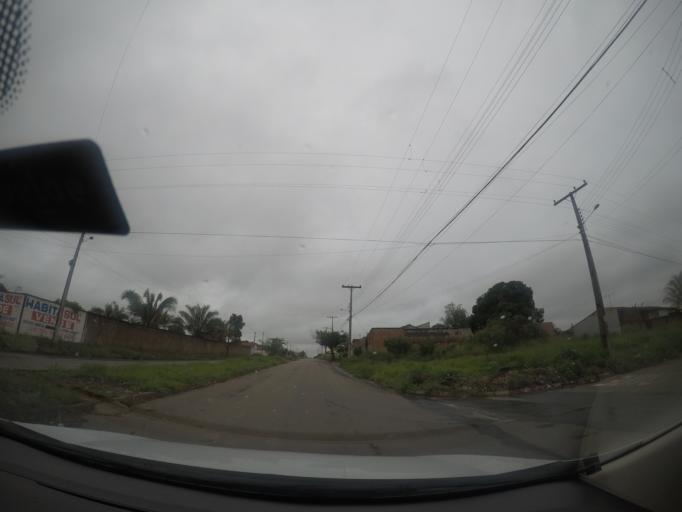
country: BR
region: Goias
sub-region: Aparecida De Goiania
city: Aparecida de Goiania
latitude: -16.7581
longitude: -49.3178
